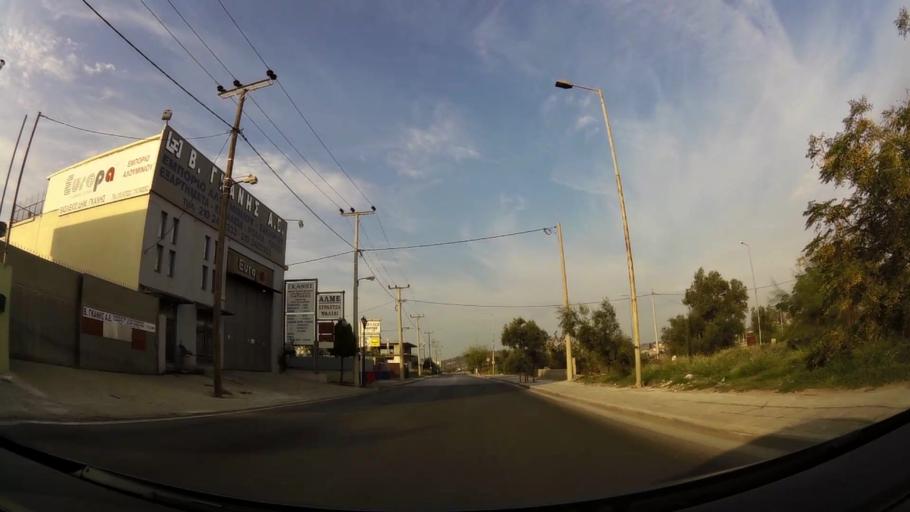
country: GR
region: Attica
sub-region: Nomarchia Dytikis Attikis
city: Ano Liosia
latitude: 38.0708
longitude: 23.6862
